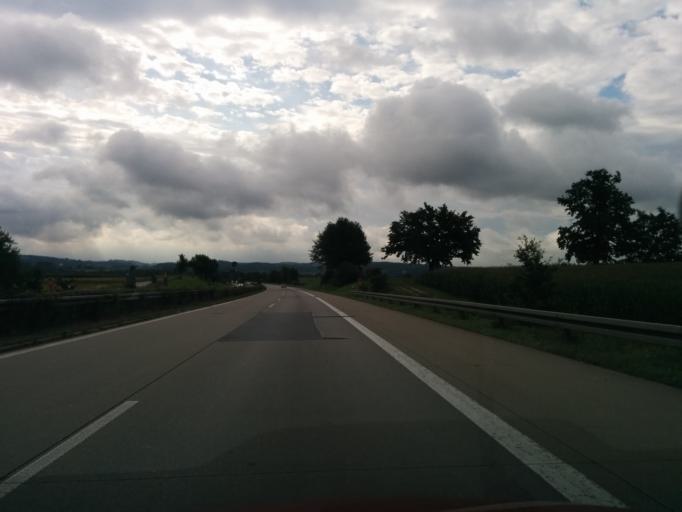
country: DE
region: Bavaria
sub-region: Lower Bavaria
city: Bogen
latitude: 48.9277
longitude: 12.7127
